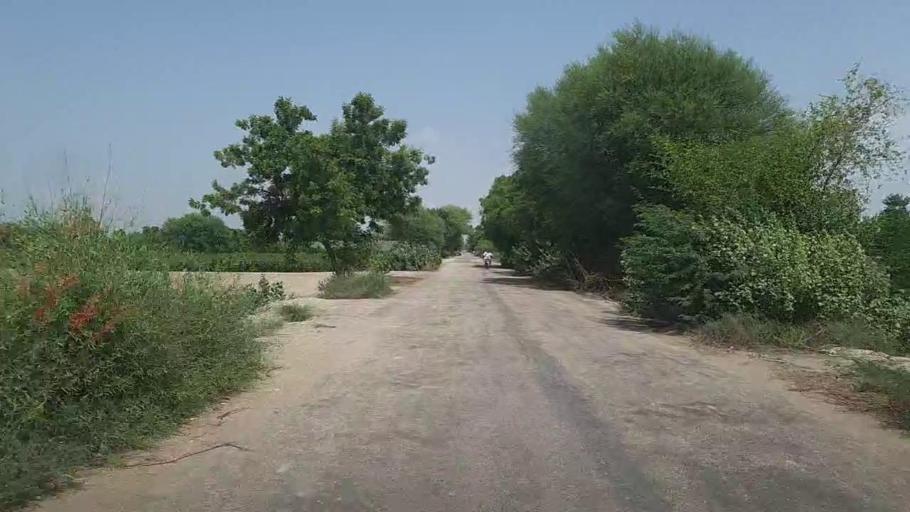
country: PK
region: Sindh
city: Pad Idan
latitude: 26.8430
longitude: 68.3452
